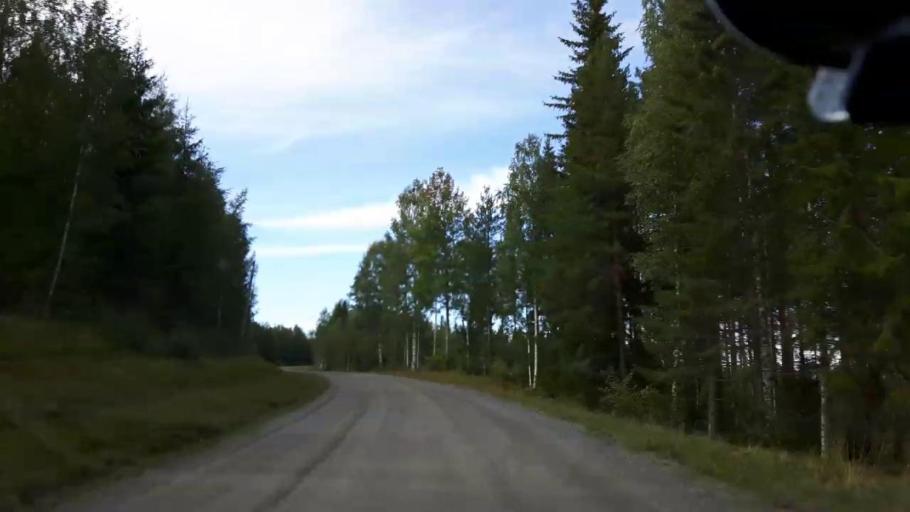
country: SE
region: Jaemtland
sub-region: Ragunda Kommun
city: Hammarstrand
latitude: 63.1276
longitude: 15.9688
